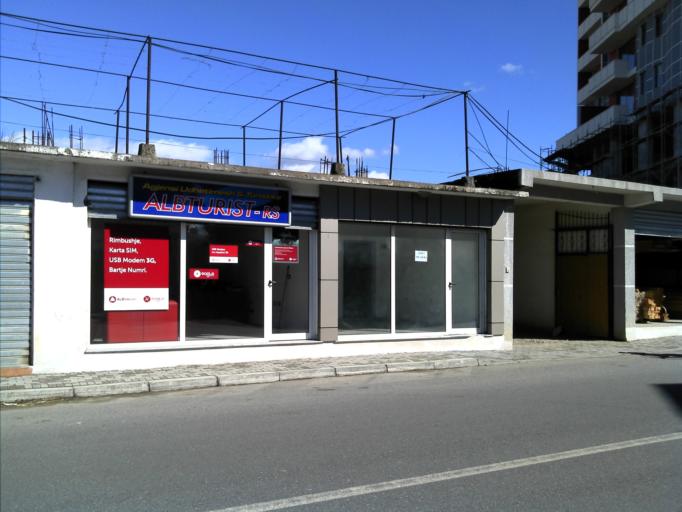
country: AL
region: Shkoder
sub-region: Rrethi i Shkodres
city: Shkoder
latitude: 42.0799
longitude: 19.5135
